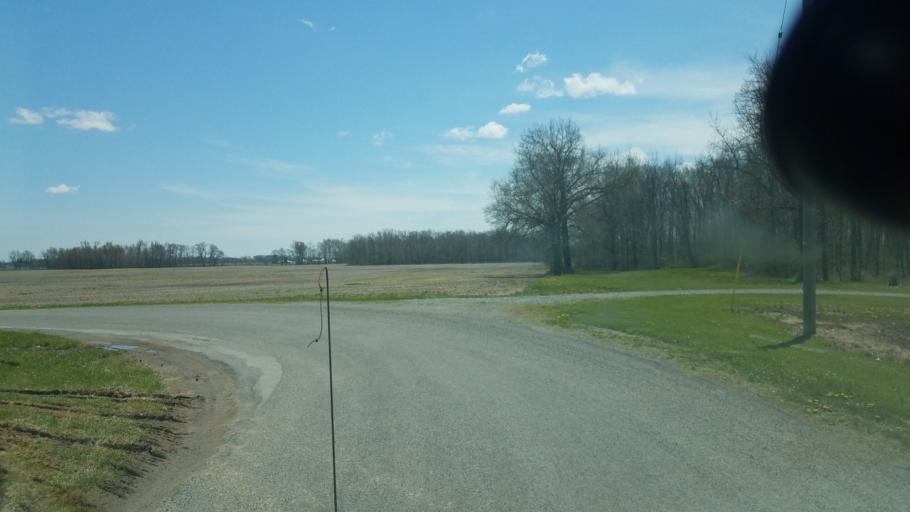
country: US
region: Ohio
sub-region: Union County
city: Richwood
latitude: 40.4903
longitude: -83.2950
